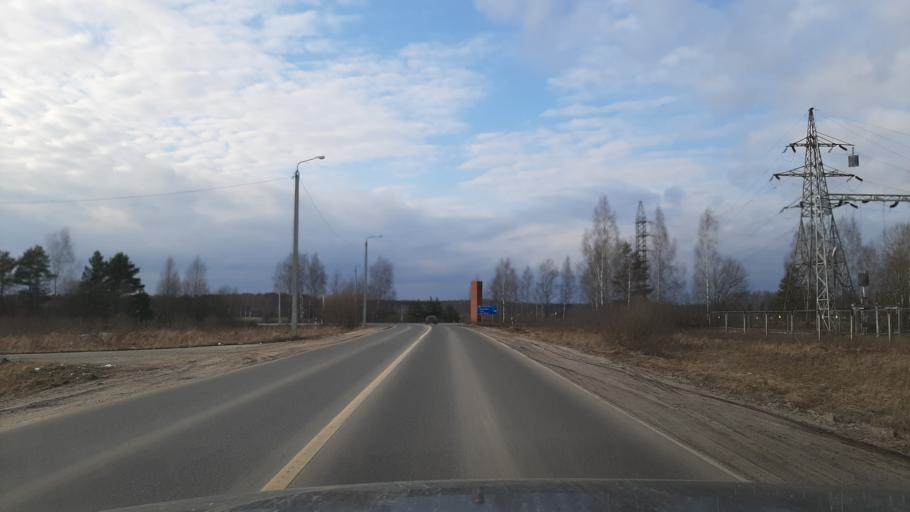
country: RU
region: Ivanovo
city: Novo-Talitsy
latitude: 56.9408
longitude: 40.7120
